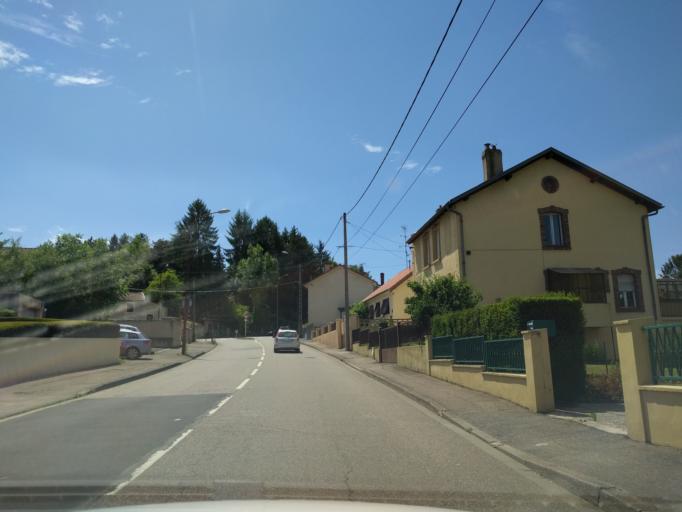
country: FR
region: Lorraine
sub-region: Departement de la Moselle
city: Woippy
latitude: 49.1377
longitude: 6.1465
